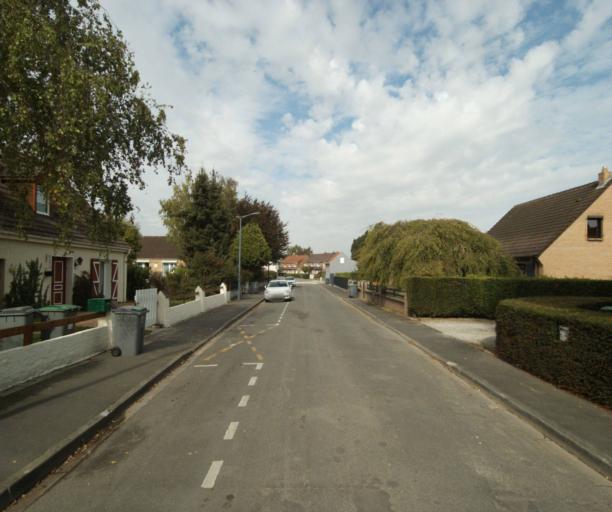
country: FR
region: Nord-Pas-de-Calais
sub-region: Departement du Nord
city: Salome
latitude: 50.5327
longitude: 2.8493
